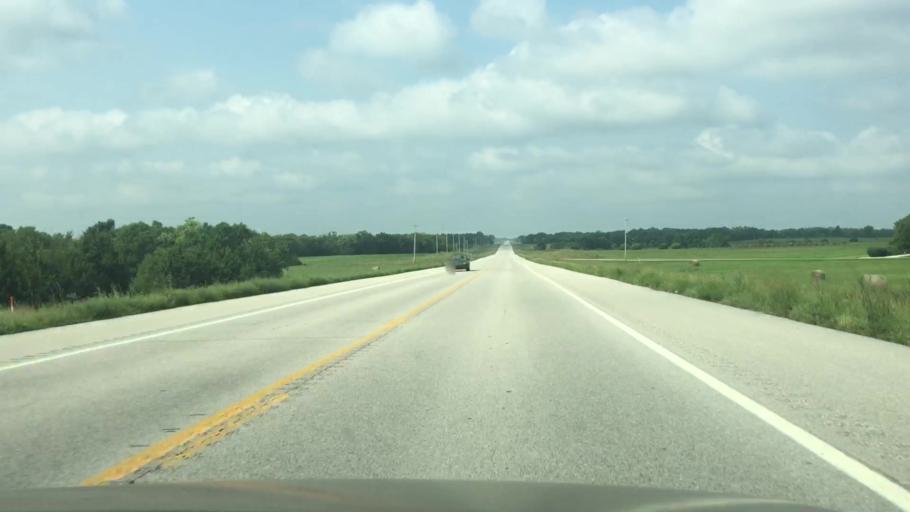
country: US
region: Kansas
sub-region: Miami County
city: Osawatomie
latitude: 38.4293
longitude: -95.0174
